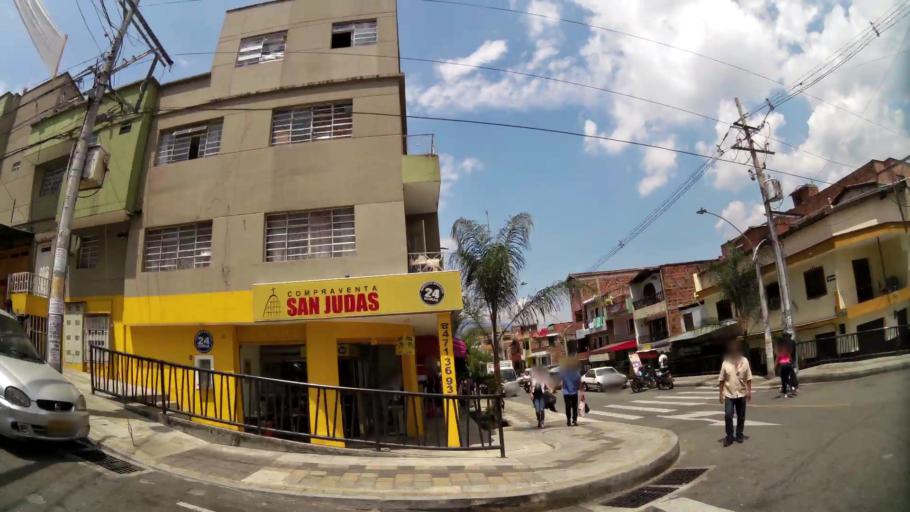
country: CO
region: Antioquia
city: Medellin
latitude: 6.2937
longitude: -75.5712
